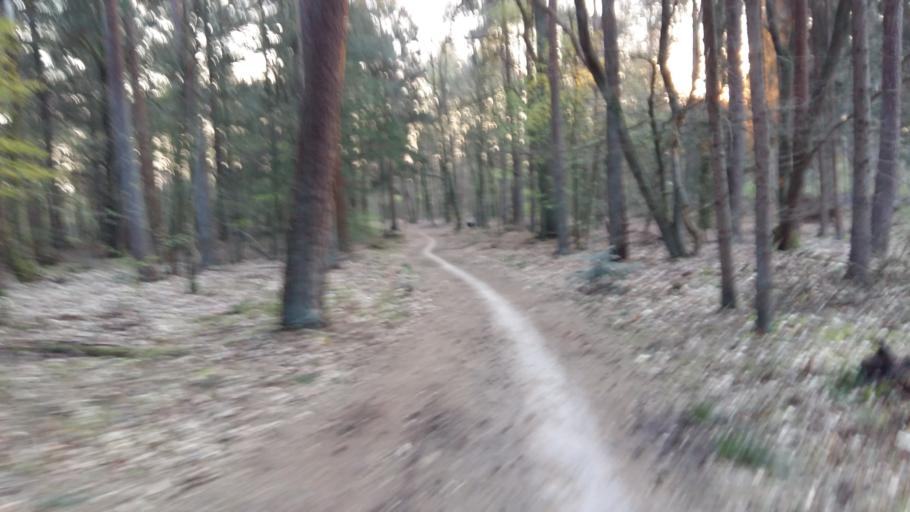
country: NL
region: Gelderland
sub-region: Gemeente Ede
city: Ede
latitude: 52.0517
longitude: 5.6927
